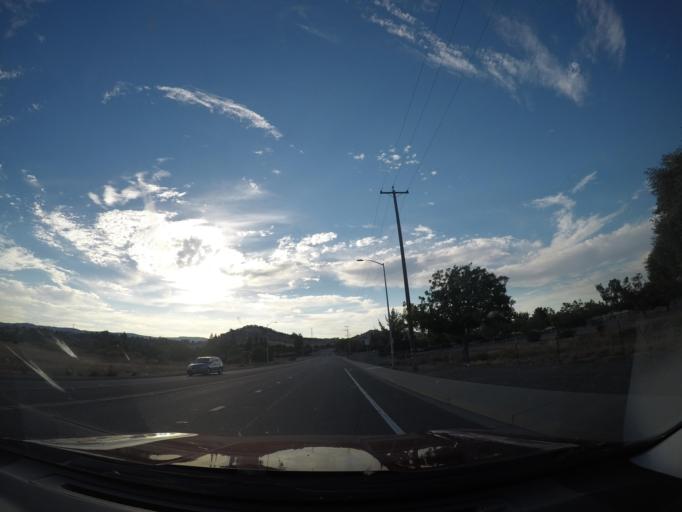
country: US
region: California
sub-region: Solano County
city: Vacaville
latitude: 38.3712
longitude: -121.9734
